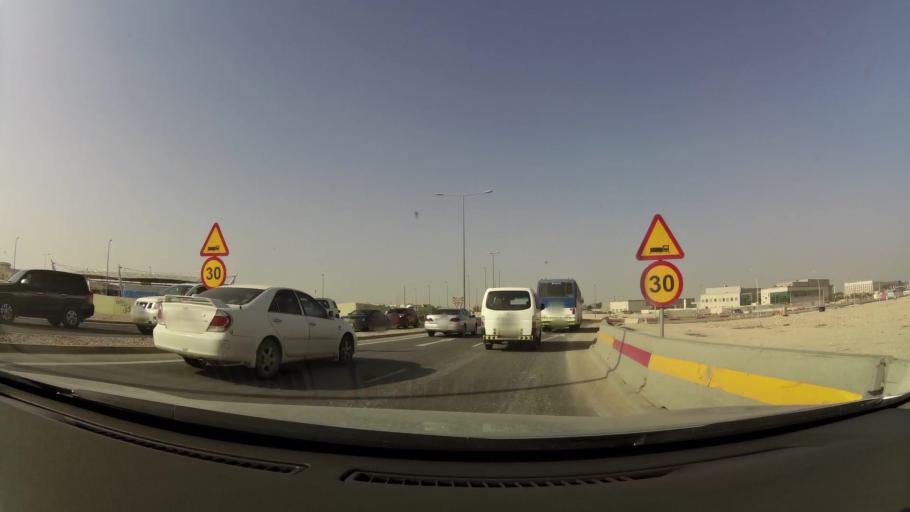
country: QA
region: Baladiyat ar Rayyan
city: Ar Rayyan
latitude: 25.3198
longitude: 51.4223
